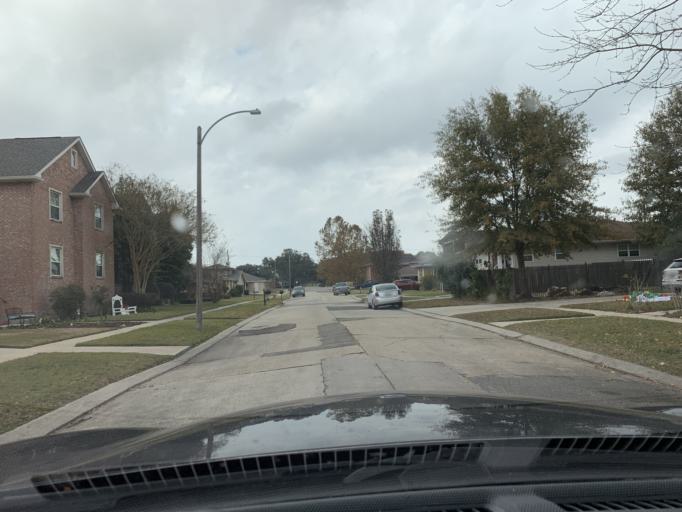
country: US
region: Louisiana
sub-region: Jefferson Parish
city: Metairie
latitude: 30.0175
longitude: -90.1000
